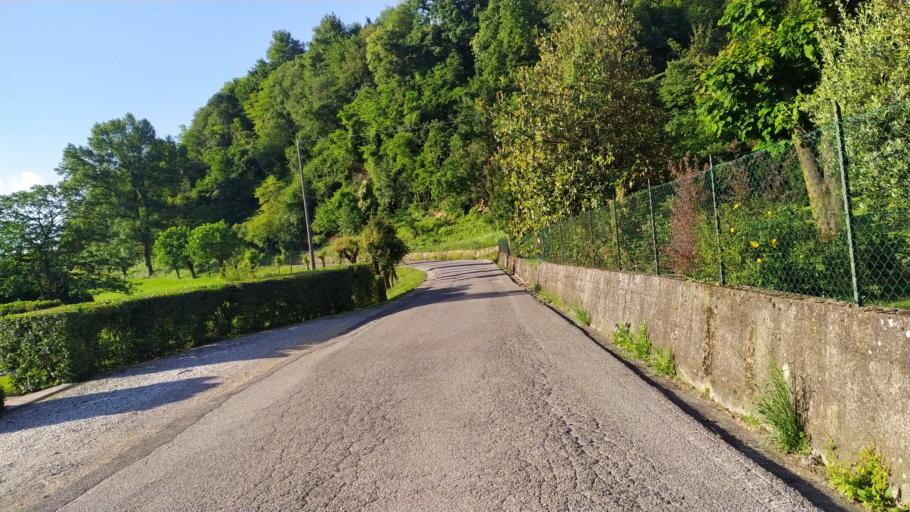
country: IT
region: Veneto
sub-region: Provincia di Vicenza
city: Malo
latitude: 45.6507
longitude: 11.4132
